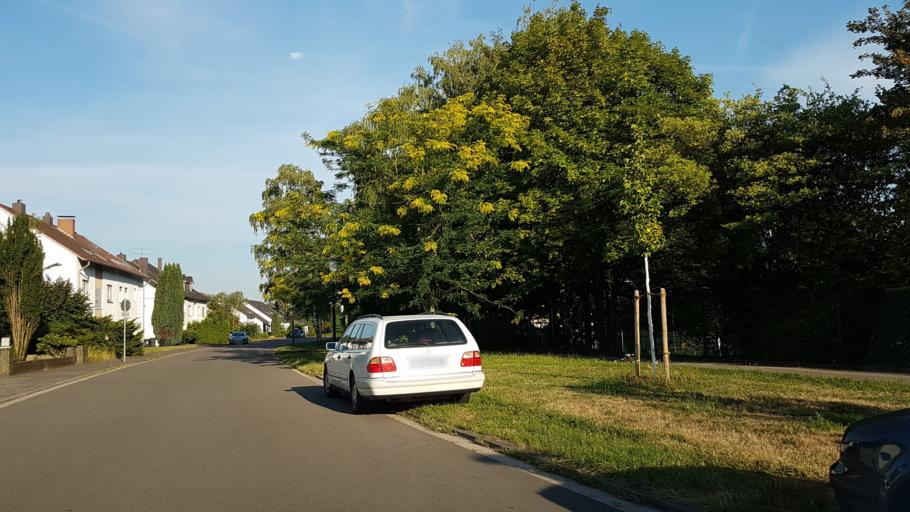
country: DE
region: Saarland
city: Homburg
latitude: 49.3146
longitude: 7.3405
